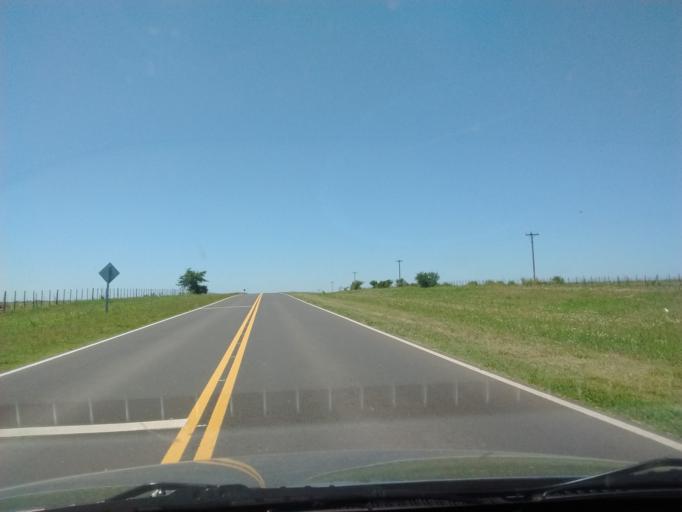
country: AR
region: Entre Rios
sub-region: Departamento de Victoria
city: Victoria
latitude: -32.7857
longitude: -59.9032
